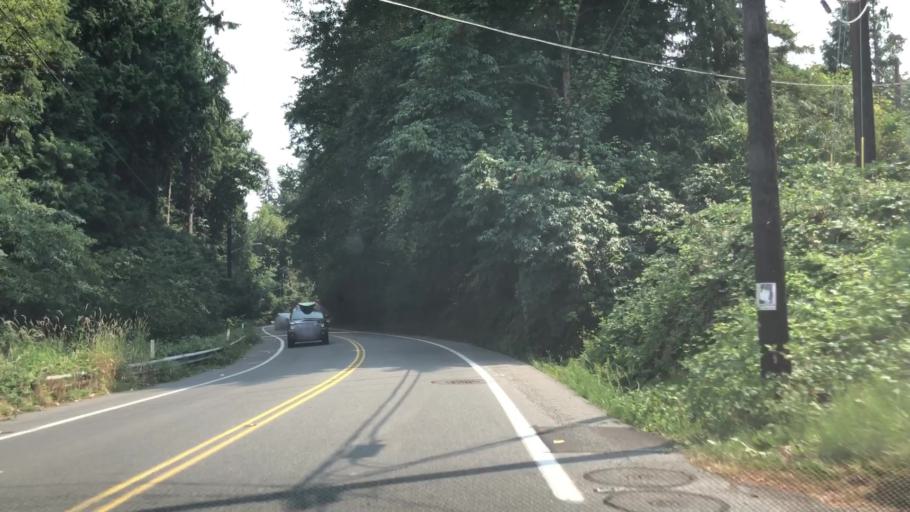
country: US
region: Washington
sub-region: King County
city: Kenmore
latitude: 47.7733
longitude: -122.2492
